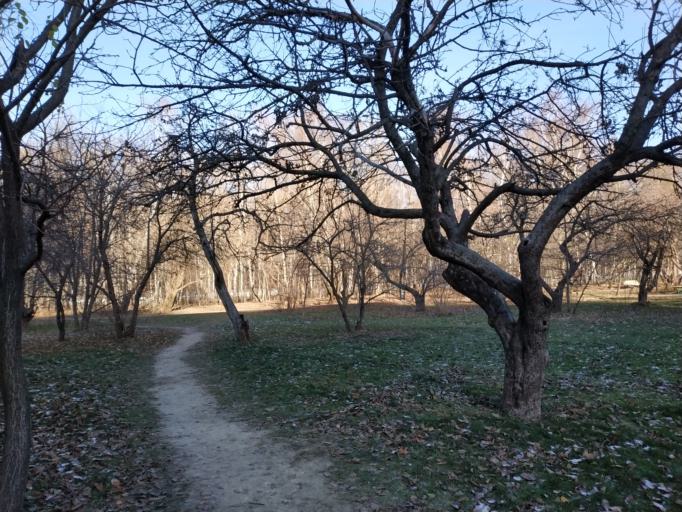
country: RU
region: Moscow
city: Biryulevo
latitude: 55.5863
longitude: 37.6935
